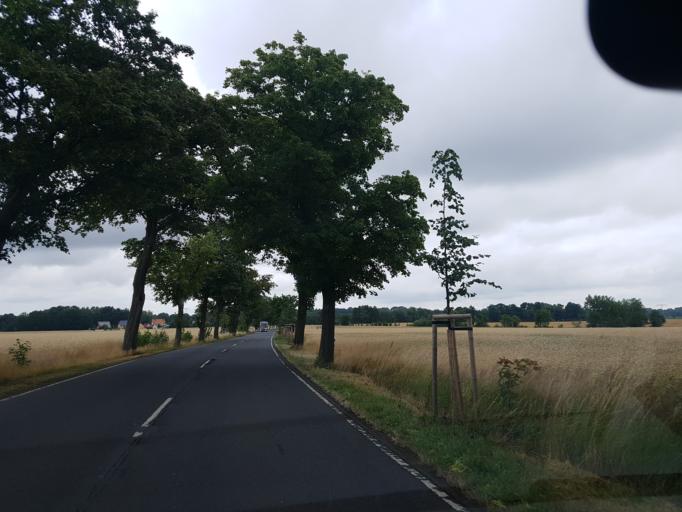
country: DE
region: Brandenburg
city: Luckau
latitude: 51.8340
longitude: 13.6875
